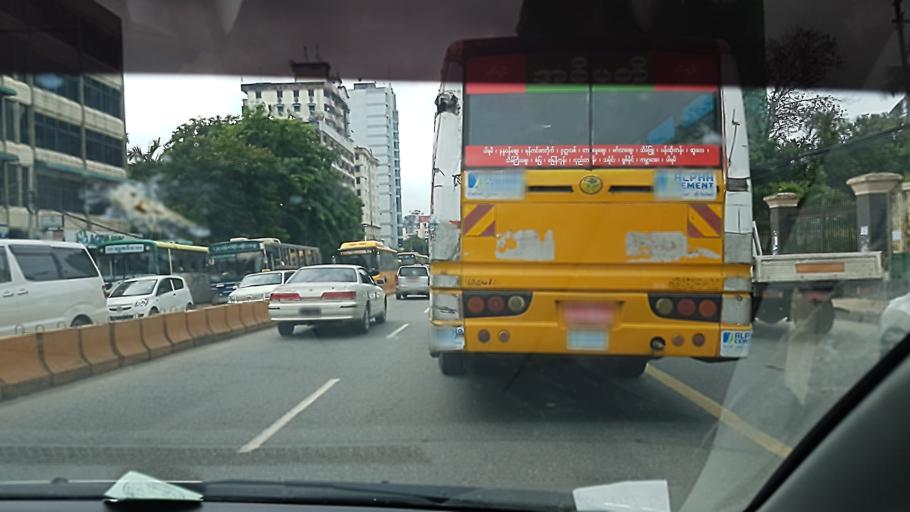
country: MM
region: Yangon
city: Yangon
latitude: 16.8065
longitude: 96.1365
